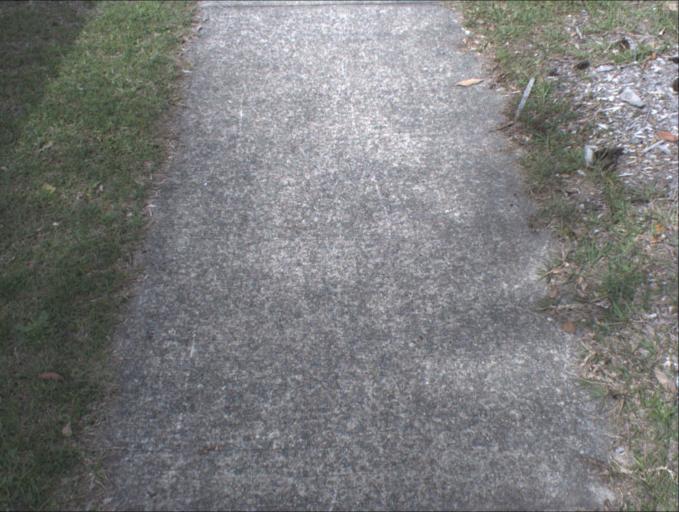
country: AU
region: Queensland
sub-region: Logan
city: Waterford West
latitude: -27.6877
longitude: 153.1000
